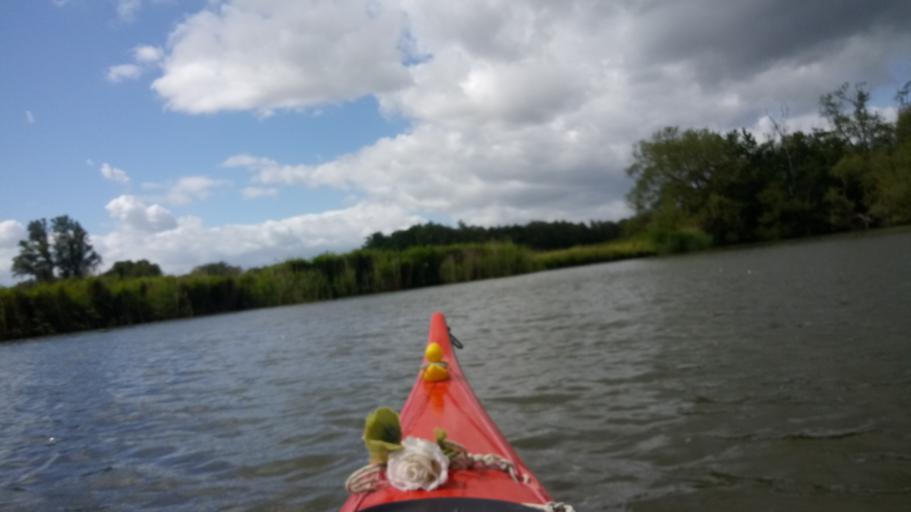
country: NL
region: North Holland
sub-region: Gemeente Enkhuizen
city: Enkhuizen
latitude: 52.7177
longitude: 5.2240
